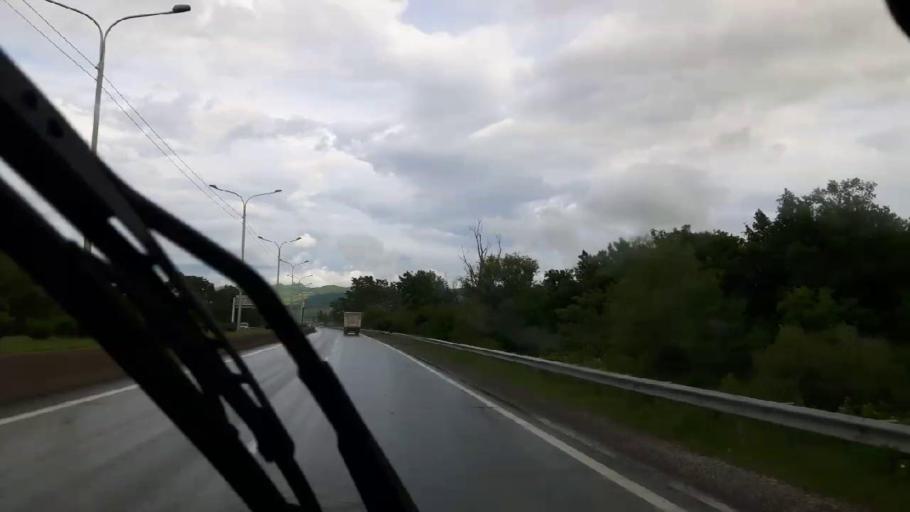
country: GE
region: Shida Kartli
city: Kaspi
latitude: 41.9109
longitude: 44.5665
